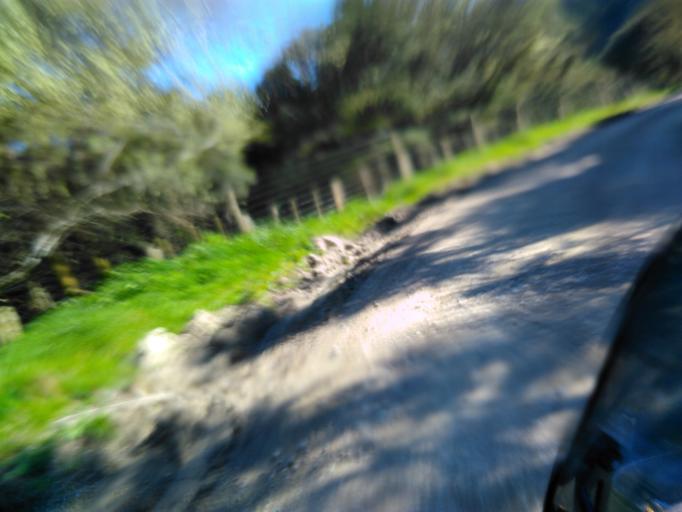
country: NZ
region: Gisborne
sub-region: Gisborne District
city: Gisborne
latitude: -38.3944
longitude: 177.6678
